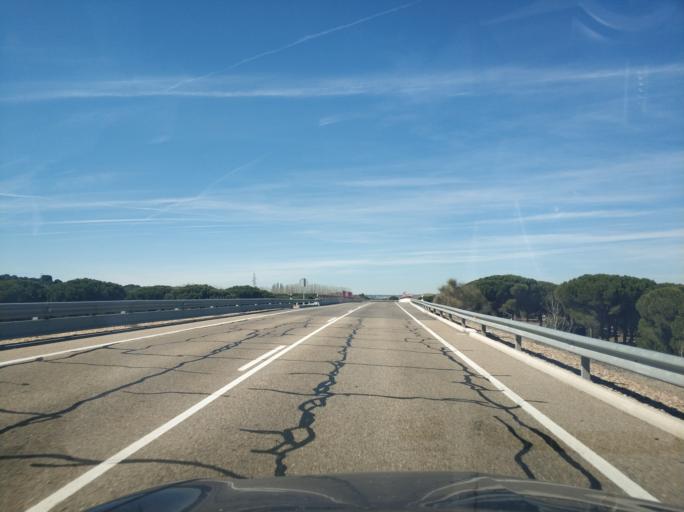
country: ES
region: Castille and Leon
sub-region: Provincia de Valladolid
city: Viana de Cega
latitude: 41.5335
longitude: -4.7551
